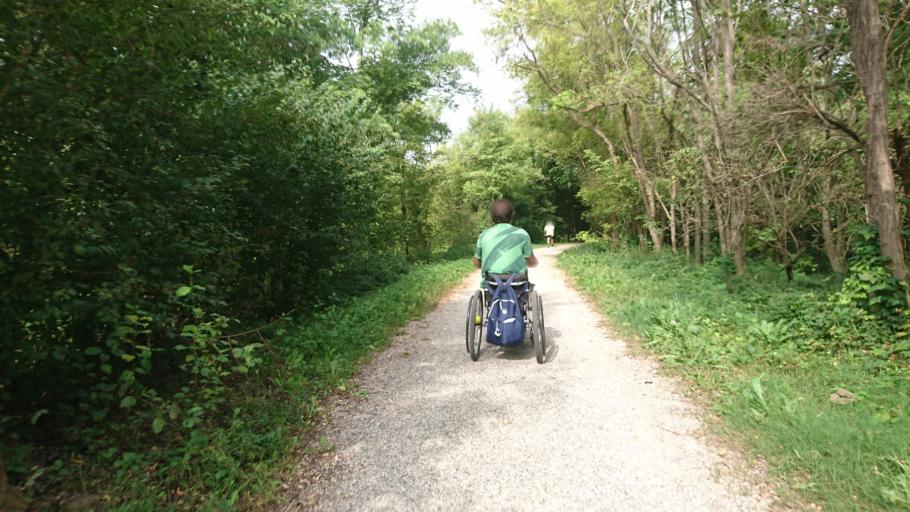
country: IT
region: Veneto
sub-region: Provincia di Padova
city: Piazzola sul Brenta
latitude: 45.5711
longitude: 11.7611
